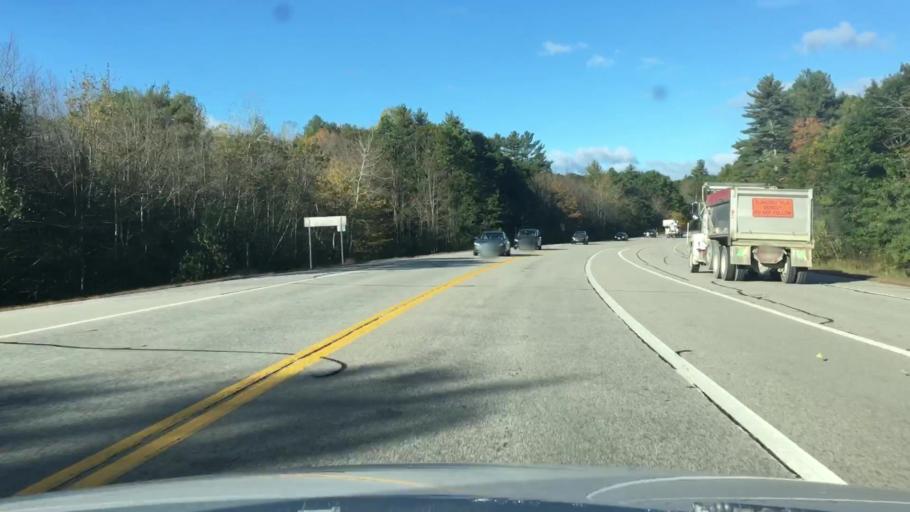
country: US
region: New Hampshire
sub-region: Strafford County
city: Durham
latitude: 43.1442
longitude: -70.9612
